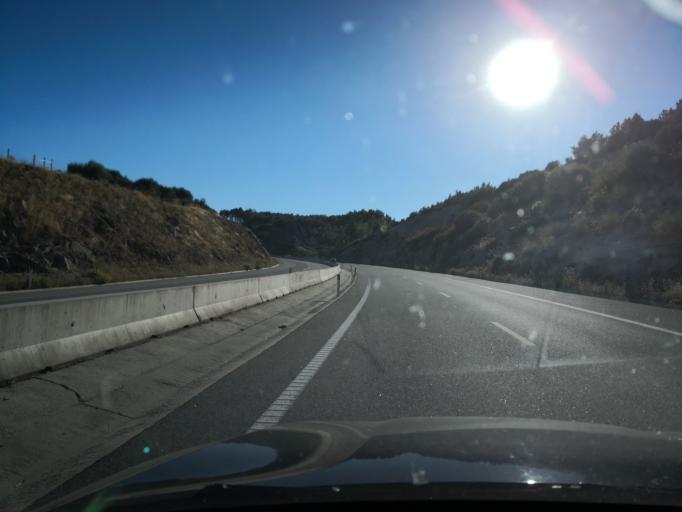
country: PT
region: Vila Real
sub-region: Murca
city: Murca
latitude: 41.3880
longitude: -7.4779
